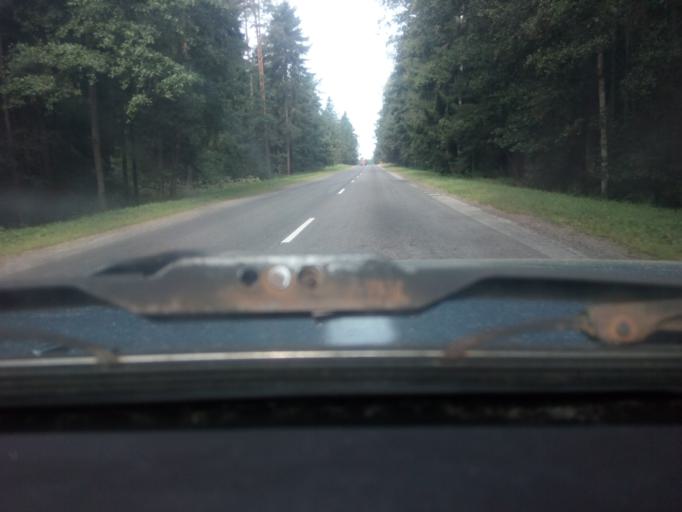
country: BY
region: Vitebsk
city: Vyerkhnyadzvinsk
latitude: 55.7961
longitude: 27.9596
